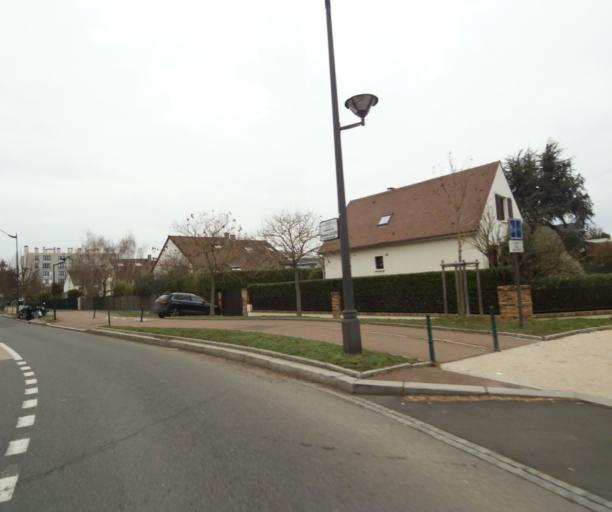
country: FR
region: Ile-de-France
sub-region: Departement des Hauts-de-Seine
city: Saint-Cloud
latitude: 48.8578
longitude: 2.1956
